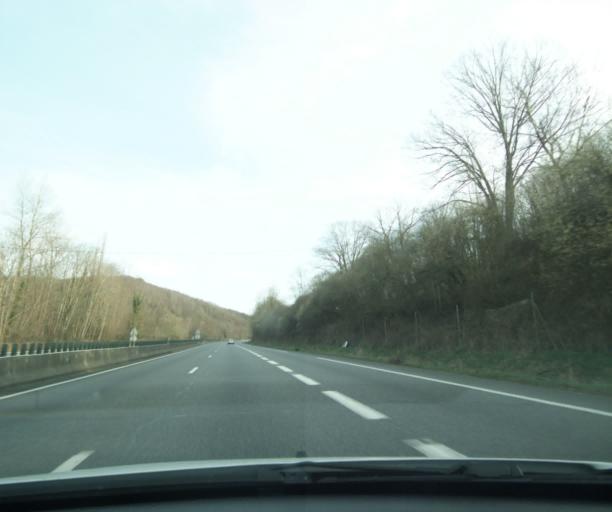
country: FR
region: Midi-Pyrenees
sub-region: Departement des Hautes-Pyrenees
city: Tournay
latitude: 43.1577
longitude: 0.2872
